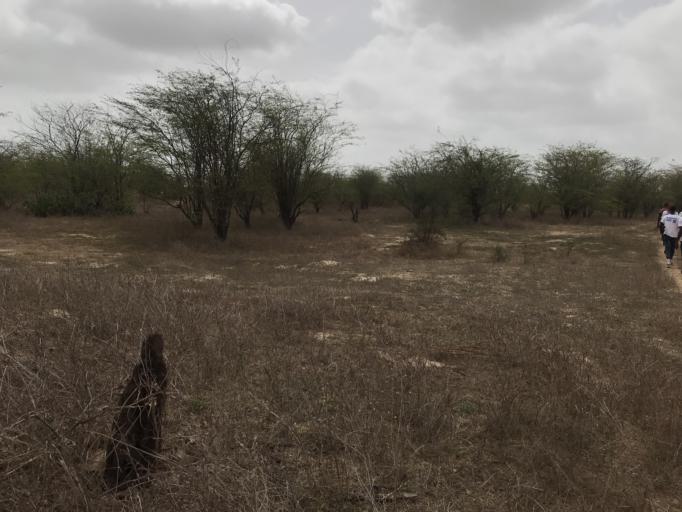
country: SN
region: Saint-Louis
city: Saint-Louis
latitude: 15.9263
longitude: -16.4546
